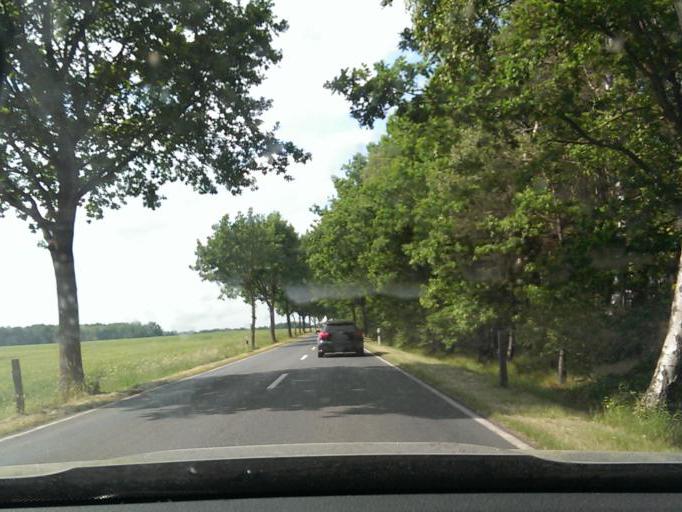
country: DE
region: Lower Saxony
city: Elze
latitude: 52.5320
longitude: 9.6883
